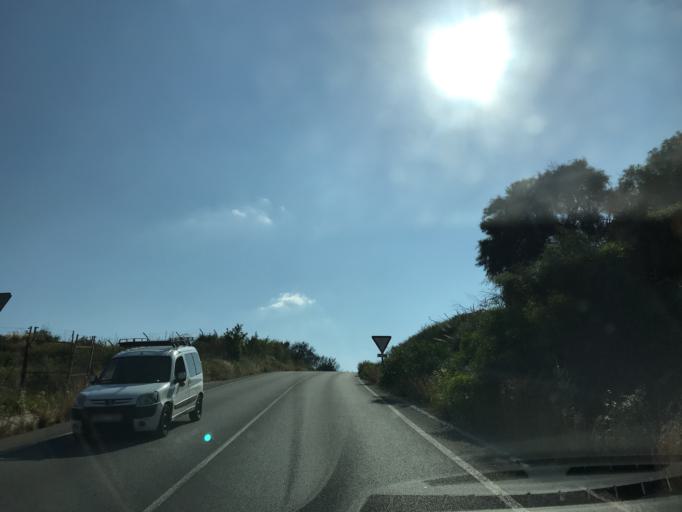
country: ES
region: Andalusia
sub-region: Provincia de Malaga
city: Benahavis
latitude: 36.5003
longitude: -5.0097
